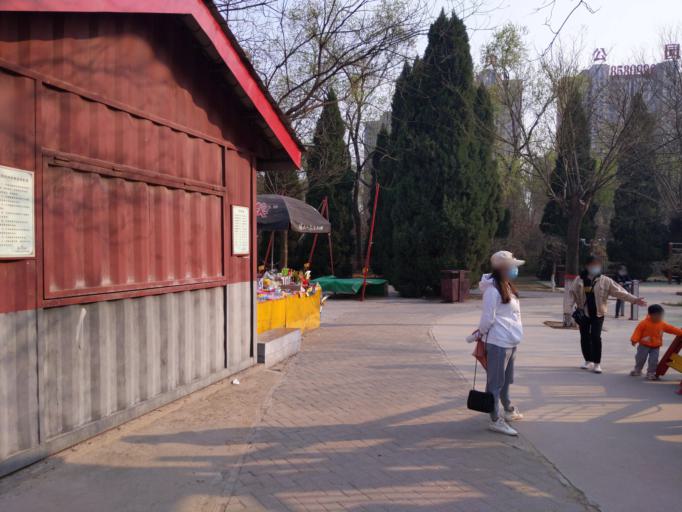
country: CN
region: Henan Sheng
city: Puyang
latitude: 35.7510
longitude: 115.0266
